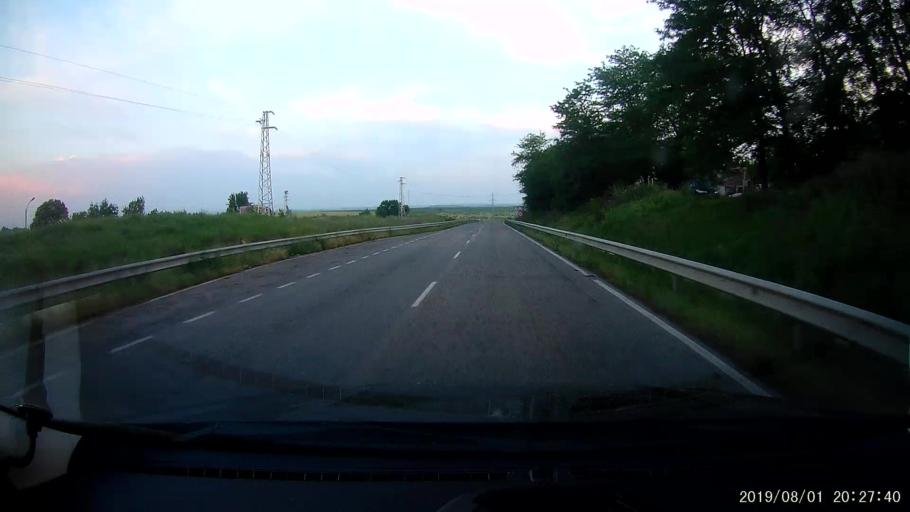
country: BG
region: Yambol
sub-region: Obshtina Elkhovo
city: Elkhovo
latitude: 42.1763
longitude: 26.5839
